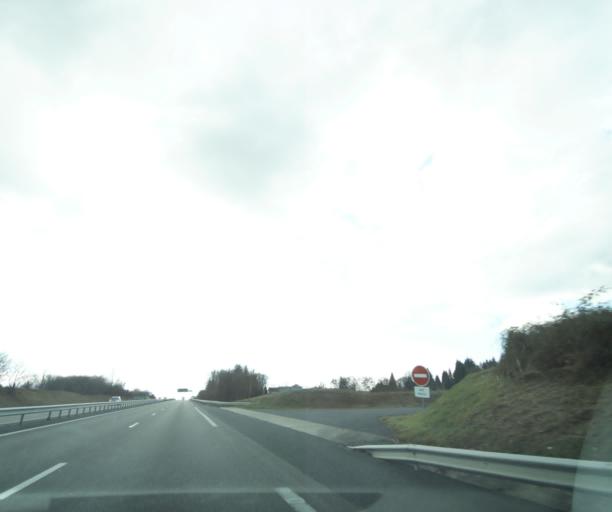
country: FR
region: Limousin
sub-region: Departement de la Correze
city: Sainte-Fereole
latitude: 45.2826
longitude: 1.5667
